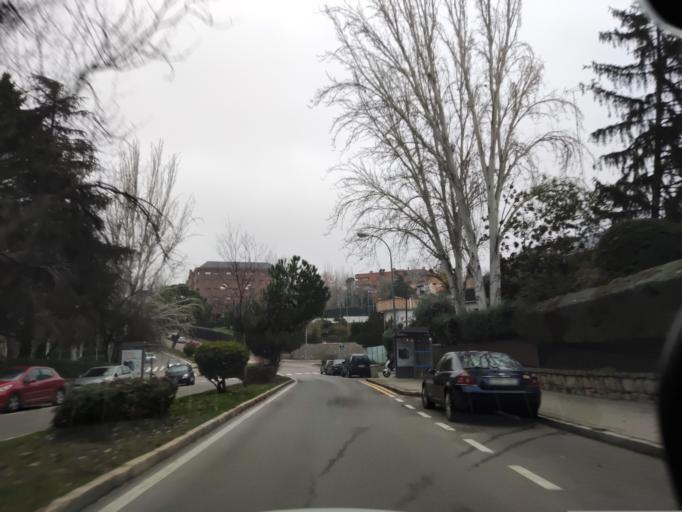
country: ES
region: Madrid
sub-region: Provincia de Madrid
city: Fuencarral-El Pardo
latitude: 40.4950
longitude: -3.7078
